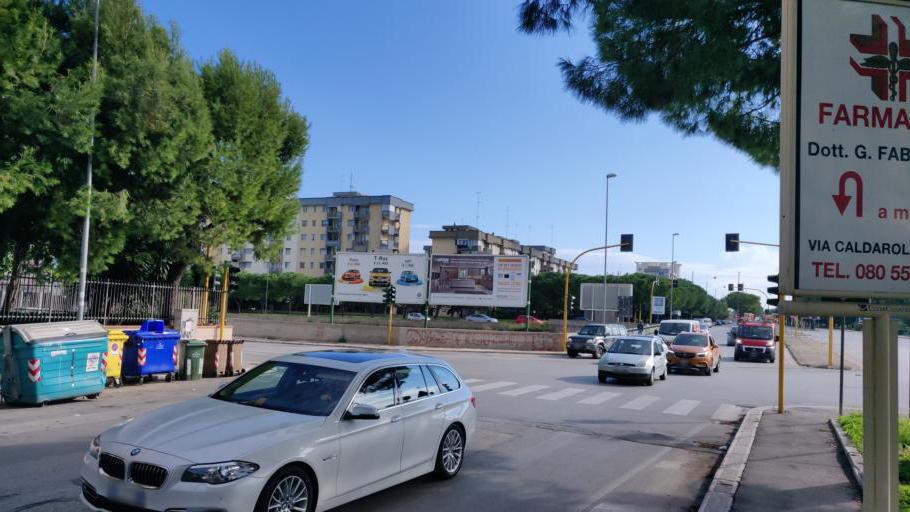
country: IT
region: Apulia
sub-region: Provincia di Bari
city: Bari
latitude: 41.1066
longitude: 16.8987
